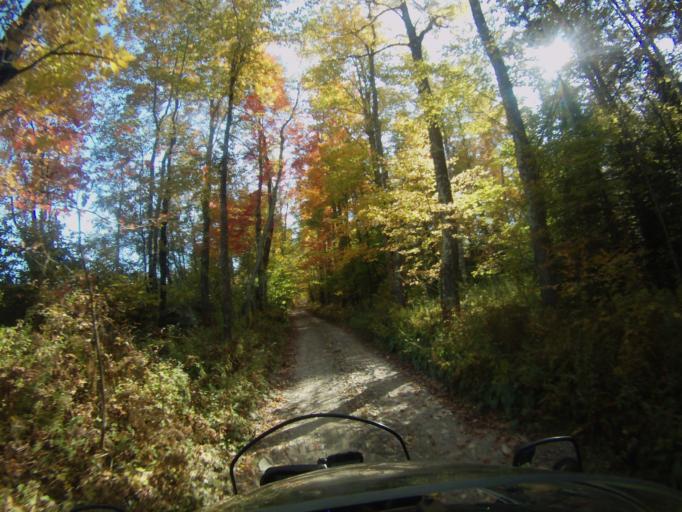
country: US
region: Vermont
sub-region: Addison County
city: Bristol
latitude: 44.1002
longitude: -72.9745
